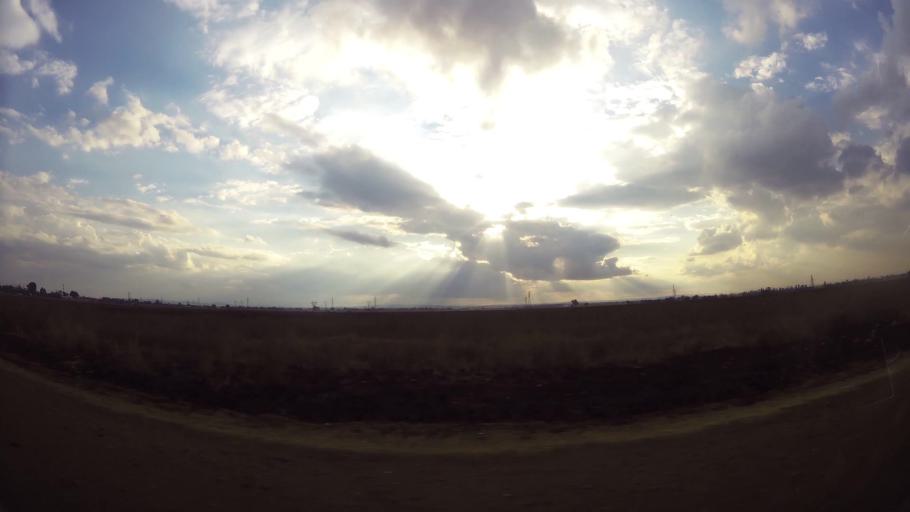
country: ZA
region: Gauteng
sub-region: Sedibeng District Municipality
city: Vanderbijlpark
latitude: -26.6716
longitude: 27.7926
